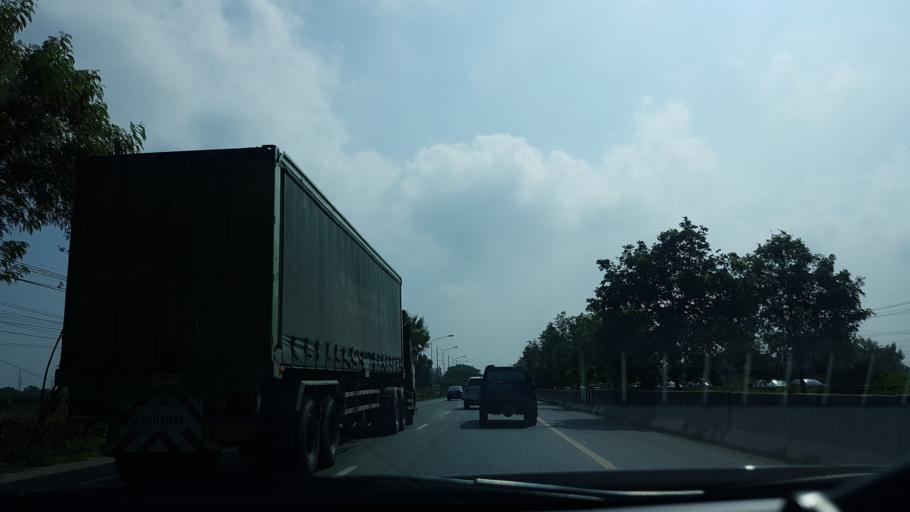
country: TH
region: Phra Nakhon Si Ayutthaya
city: Bang Pa-in
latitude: 14.1694
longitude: 100.5981
